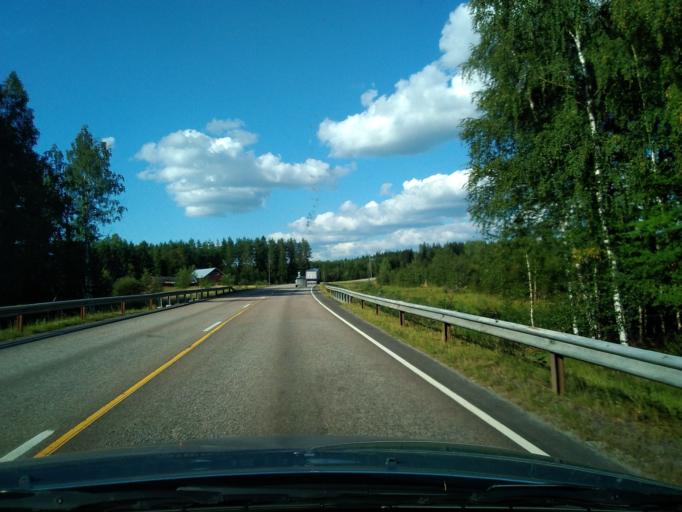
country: FI
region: Pirkanmaa
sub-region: Ylae-Pirkanmaa
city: Maenttae
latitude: 62.0956
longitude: 24.7282
